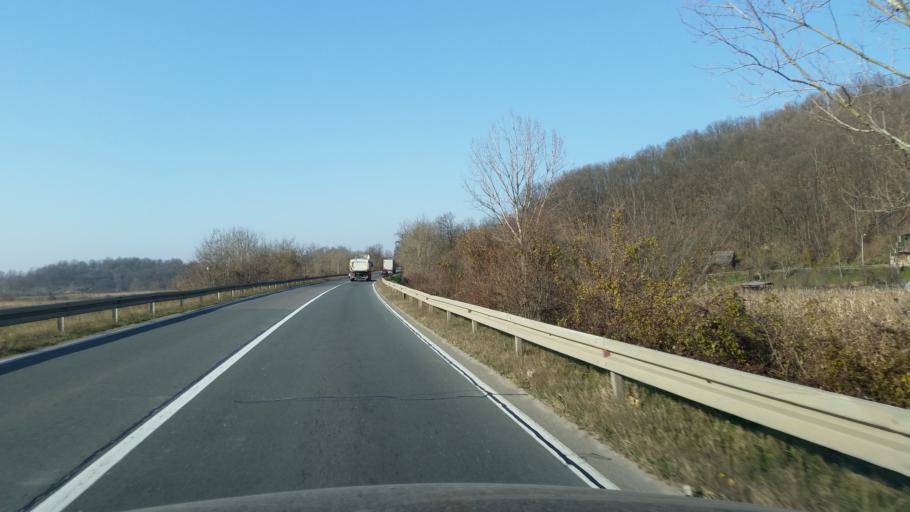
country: RS
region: Central Serbia
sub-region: Kolubarski Okrug
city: Lajkovac
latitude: 44.3445
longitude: 20.1999
